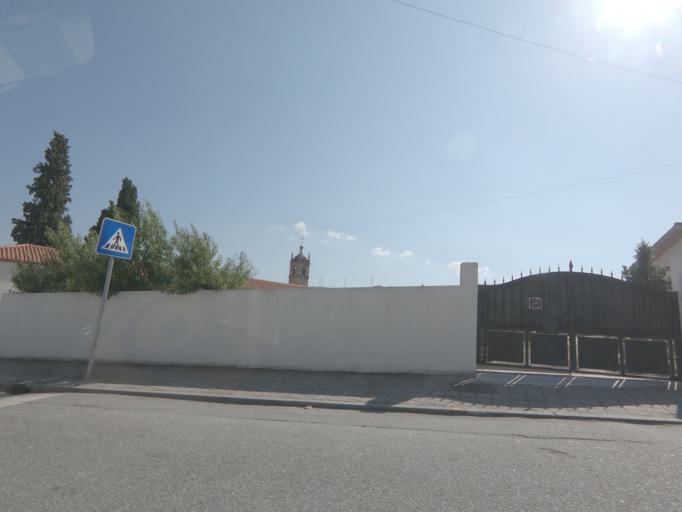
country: PT
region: Viseu
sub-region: Moimenta da Beira
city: Moimenta da Beira
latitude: 40.9842
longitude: -7.6135
